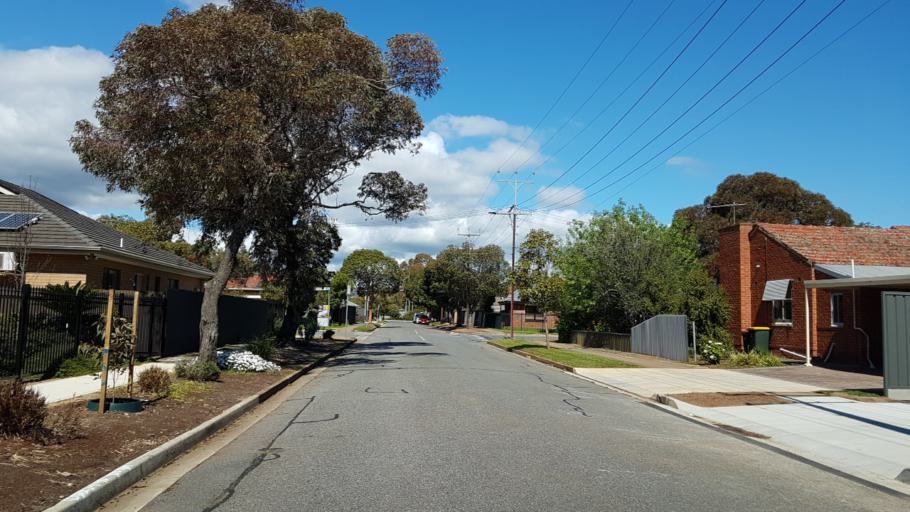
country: AU
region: South Australia
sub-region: Marion
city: Plympton Park
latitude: -34.9972
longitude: 138.5521
